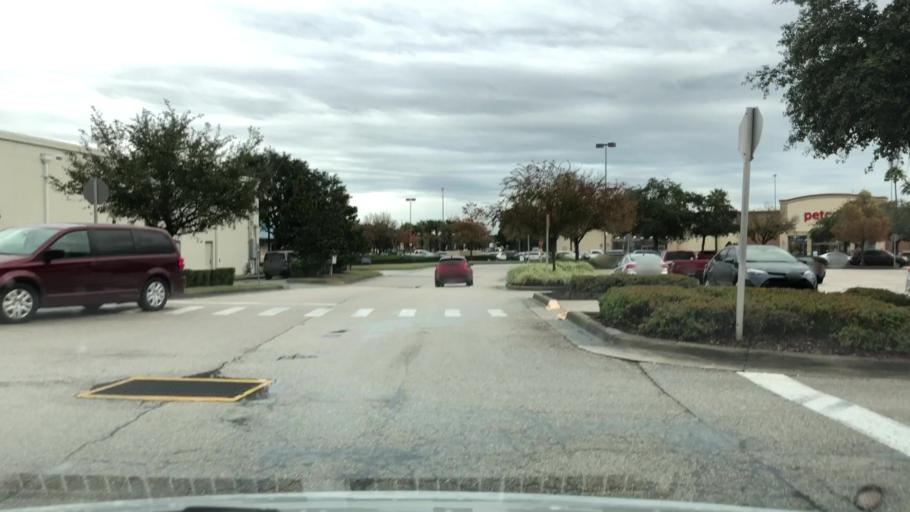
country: US
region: Florida
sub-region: Seminole County
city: Lake Mary
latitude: 28.7998
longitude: -81.3338
